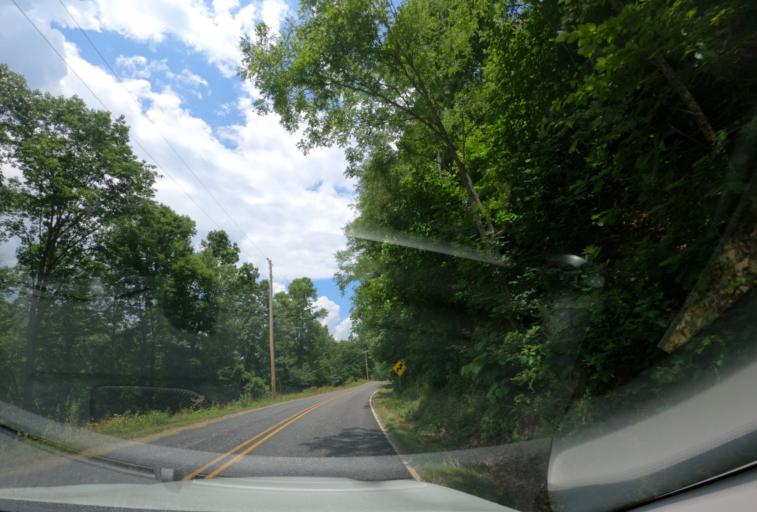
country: US
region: North Carolina
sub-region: Haywood County
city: Hazelwood
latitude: 35.3976
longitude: -82.8967
